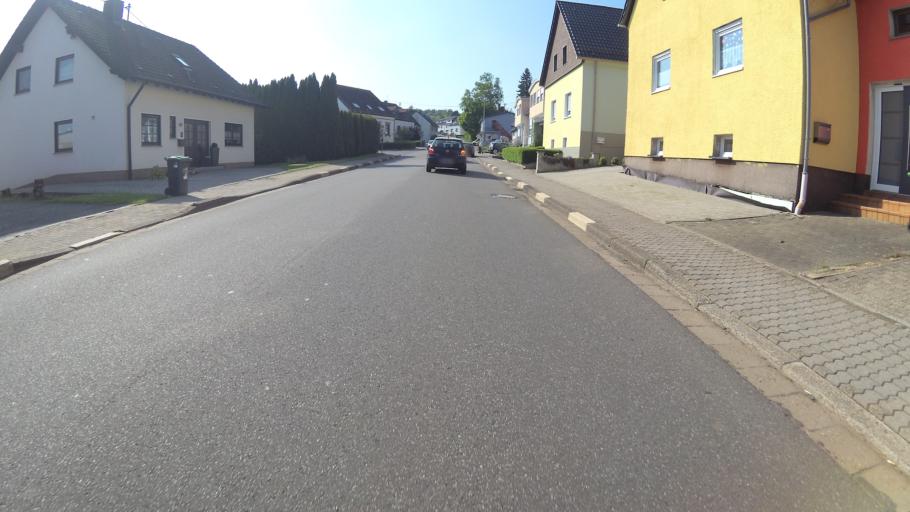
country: DE
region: Saarland
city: Illingen
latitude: 49.3830
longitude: 7.0192
